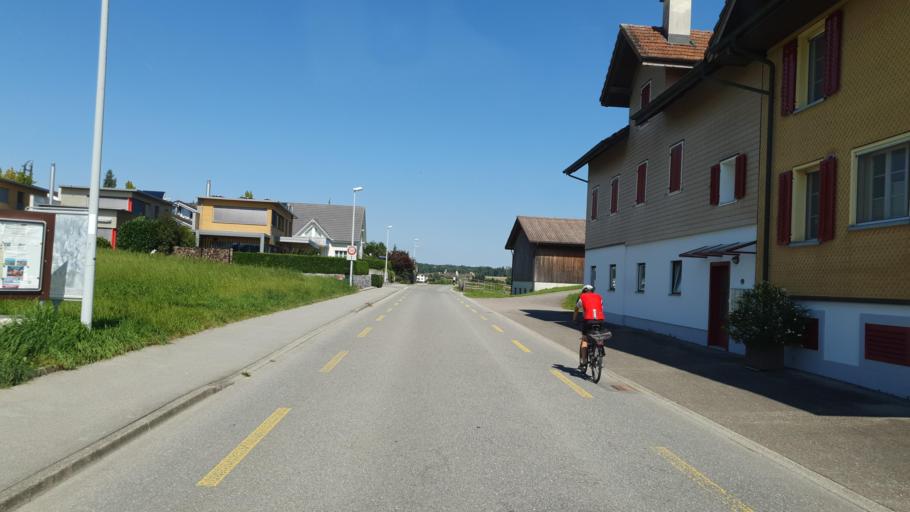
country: CH
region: Lucerne
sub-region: Hochdorf District
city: Ballwil
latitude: 47.1362
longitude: 8.3229
